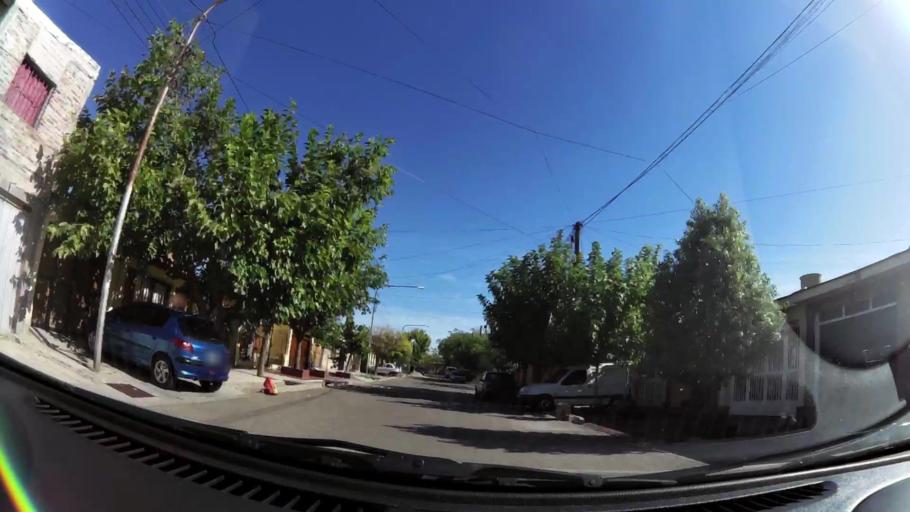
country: AR
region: Mendoza
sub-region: Departamento de Godoy Cruz
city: Godoy Cruz
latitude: -32.9408
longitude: -68.8108
